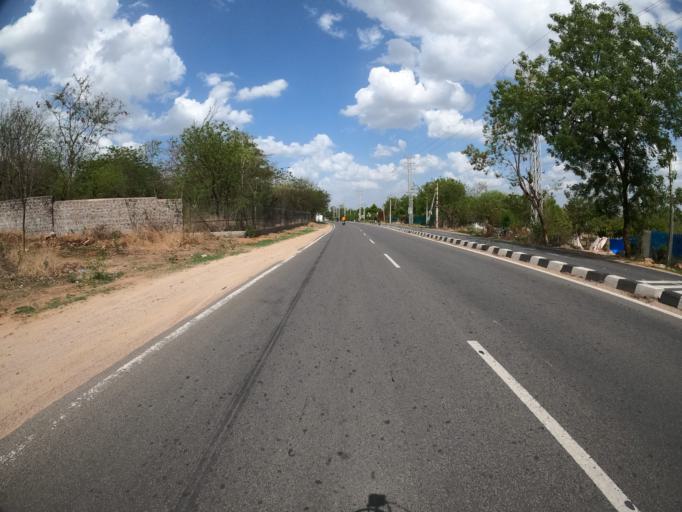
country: IN
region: Telangana
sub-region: Rangareddi
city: Sriramnagar
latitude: 17.3538
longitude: 78.3359
